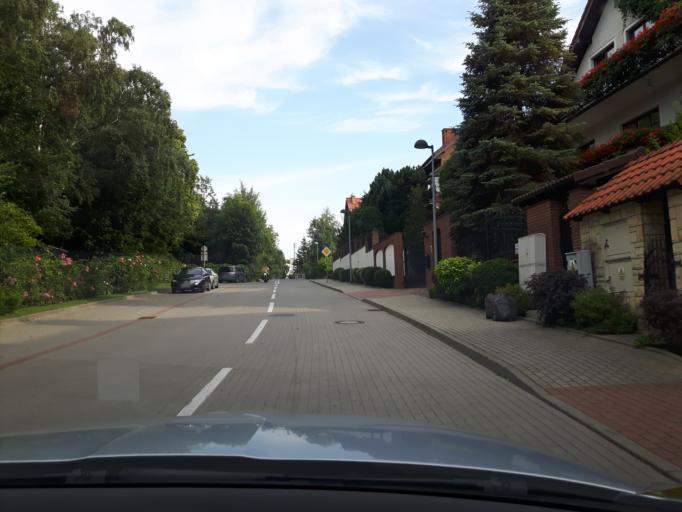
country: PL
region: Pomeranian Voivodeship
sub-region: Gdynia
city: Gdynia
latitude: 54.5031
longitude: 18.5467
